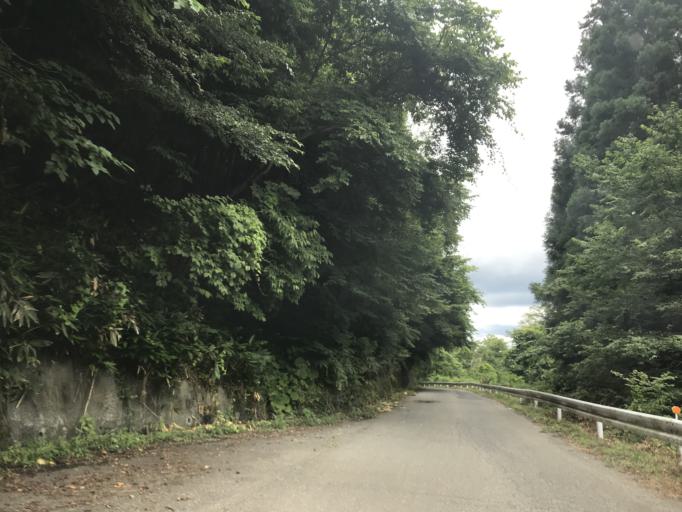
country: JP
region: Iwate
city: Ichinoseki
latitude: 38.9697
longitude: 140.9260
